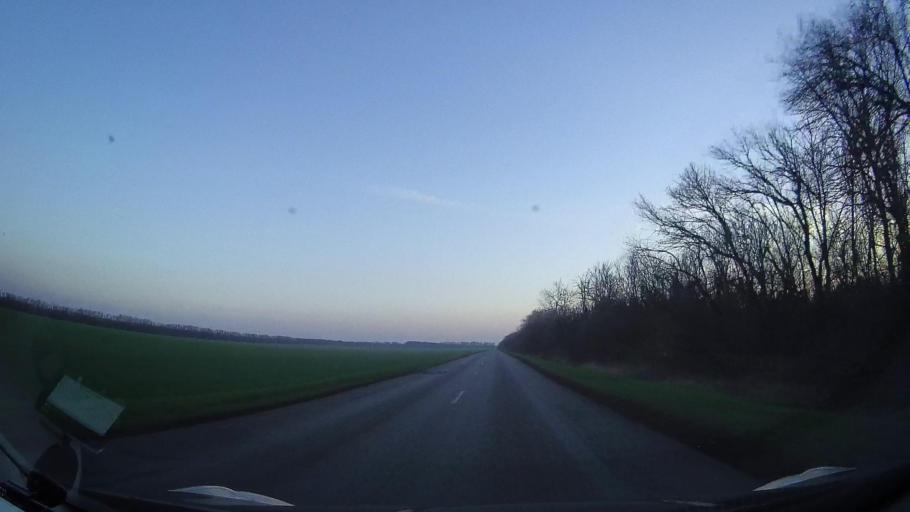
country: RU
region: Rostov
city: Zernograd
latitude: 46.9792
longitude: 40.3915
